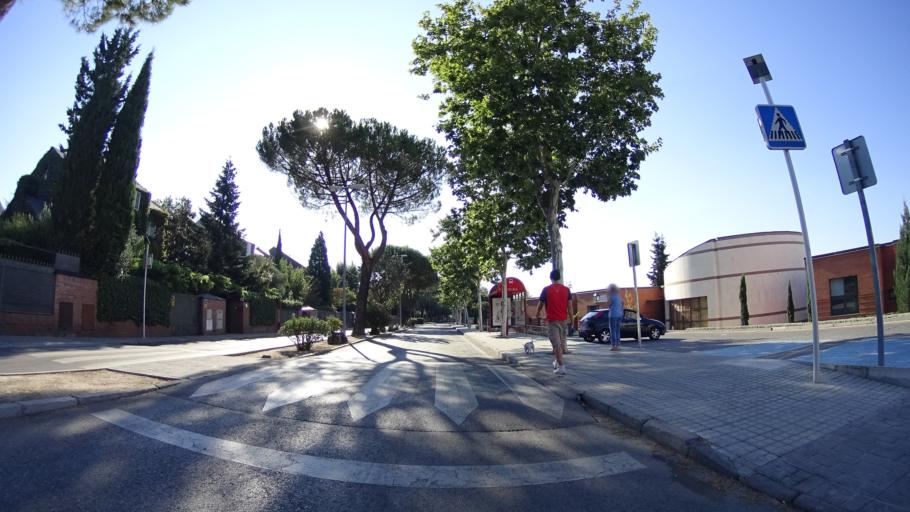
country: ES
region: Madrid
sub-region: Provincia de Madrid
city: Torrelodones
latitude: 40.5814
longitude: -3.9300
